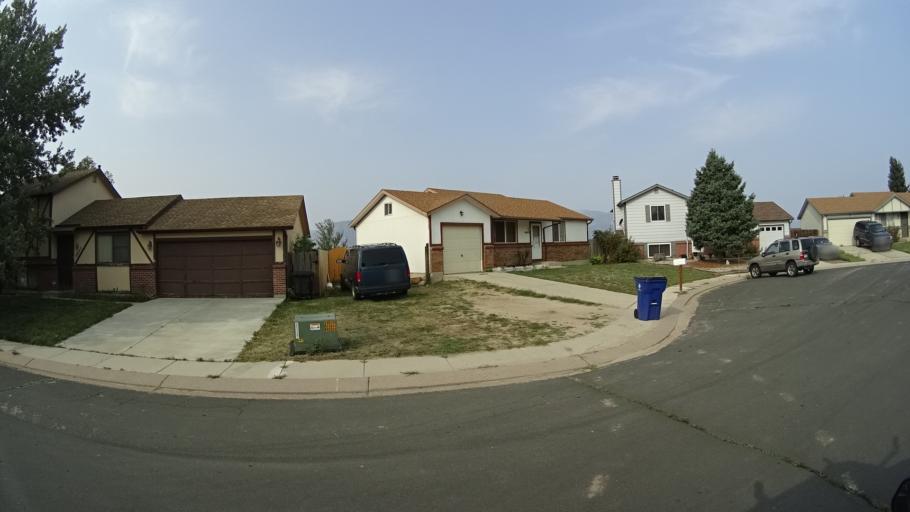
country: US
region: Colorado
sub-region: El Paso County
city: Stratmoor
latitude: 38.8040
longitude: -104.7382
